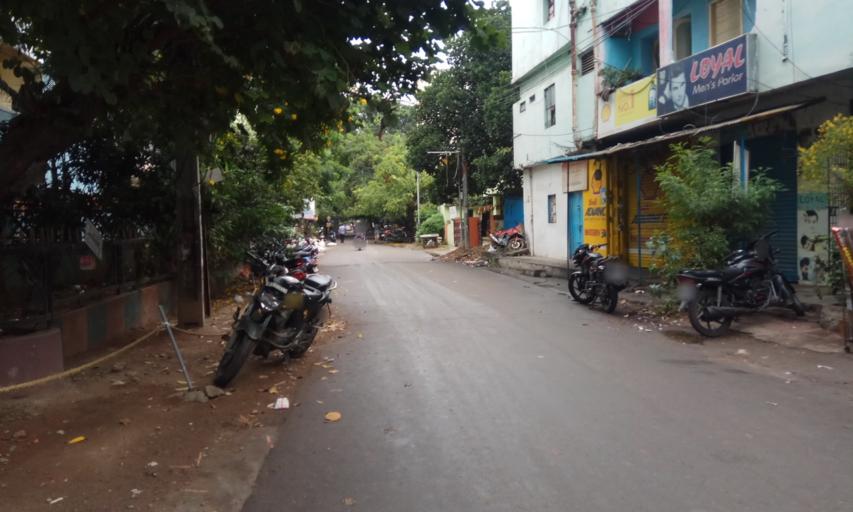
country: IN
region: Telangana
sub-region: Hyderabad
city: Hyderabad
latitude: 17.4355
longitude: 78.4389
